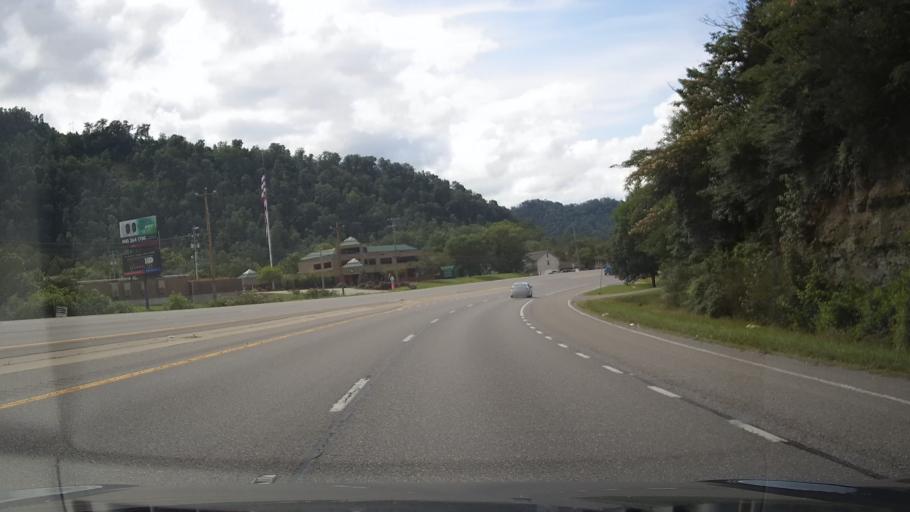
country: US
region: Kentucky
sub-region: Pike County
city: Coal Run Village
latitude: 37.5307
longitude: -82.6255
